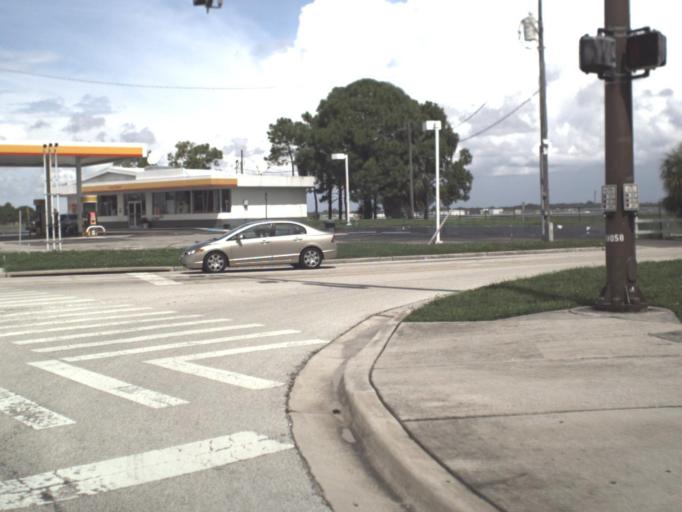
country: US
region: Florida
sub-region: Manatee County
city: Whitfield
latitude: 27.3860
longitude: -82.5581
